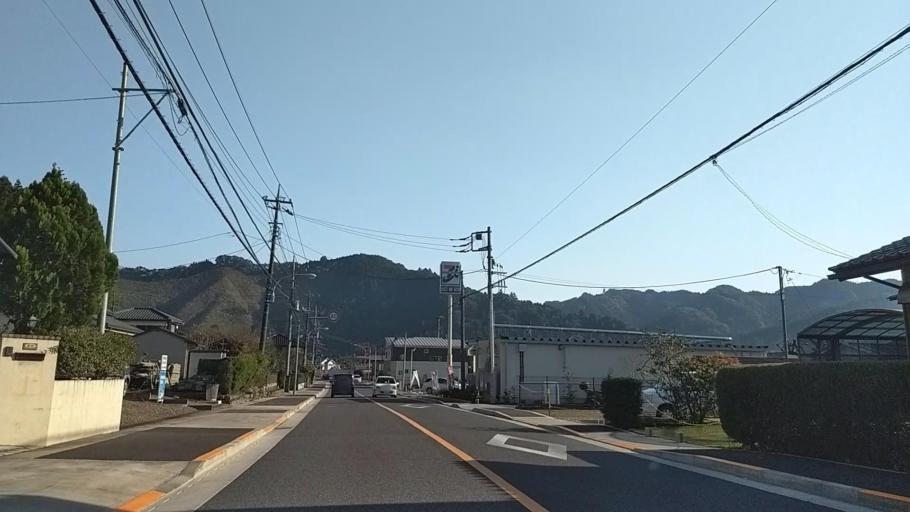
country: JP
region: Tokyo
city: Ome
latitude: 35.7843
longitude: 139.2324
